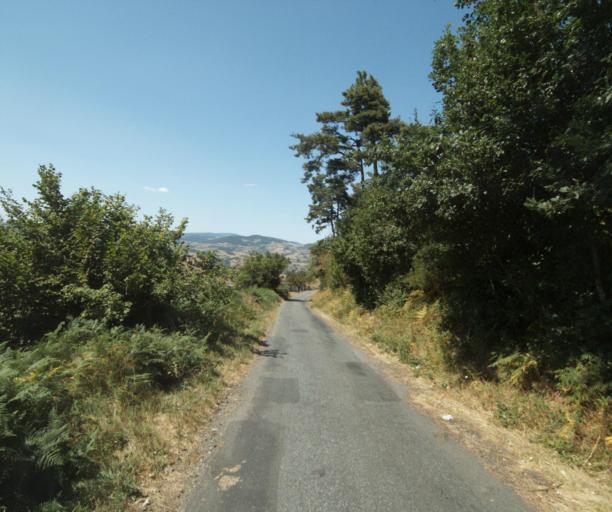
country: FR
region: Rhone-Alpes
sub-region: Departement du Rhone
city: Courzieu
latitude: 45.7189
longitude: 4.5485
